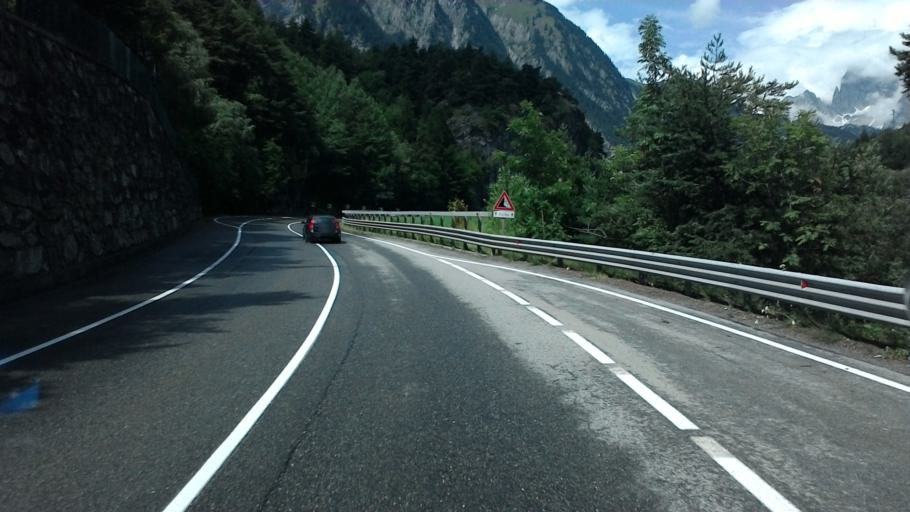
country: IT
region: Aosta Valley
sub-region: Valle d'Aosta
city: Pre Saint Didier
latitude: 45.7625
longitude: 7.0034
